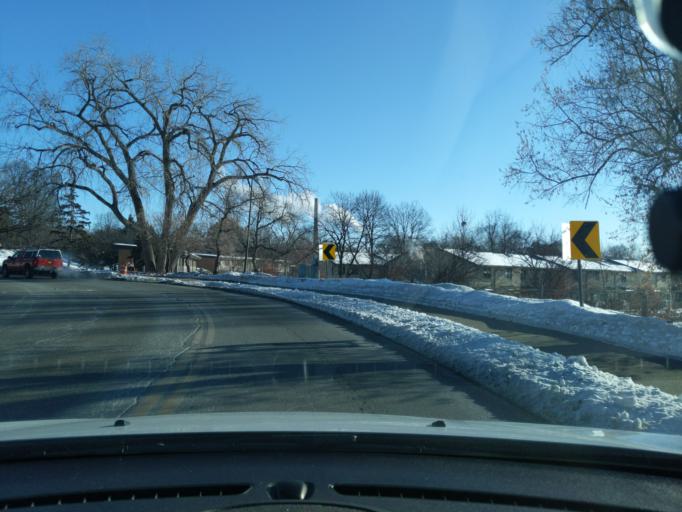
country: US
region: Minnesota
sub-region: Ramsey County
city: Falcon Heights
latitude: 44.9782
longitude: -93.1876
